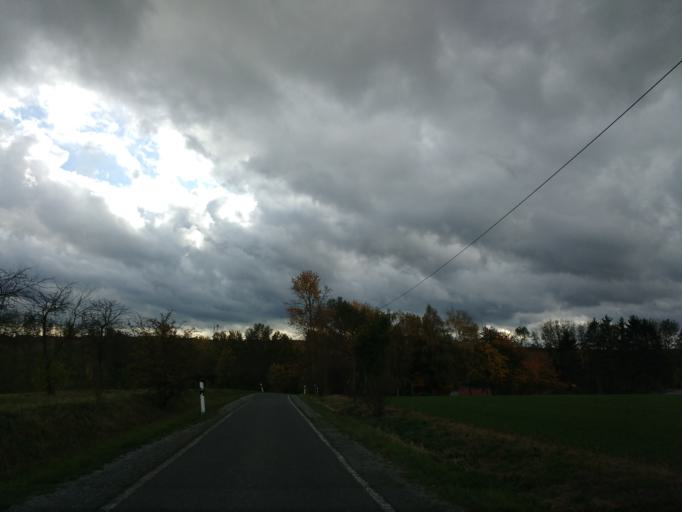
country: DE
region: Thuringia
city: Worbis
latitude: 51.4056
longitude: 10.3589
